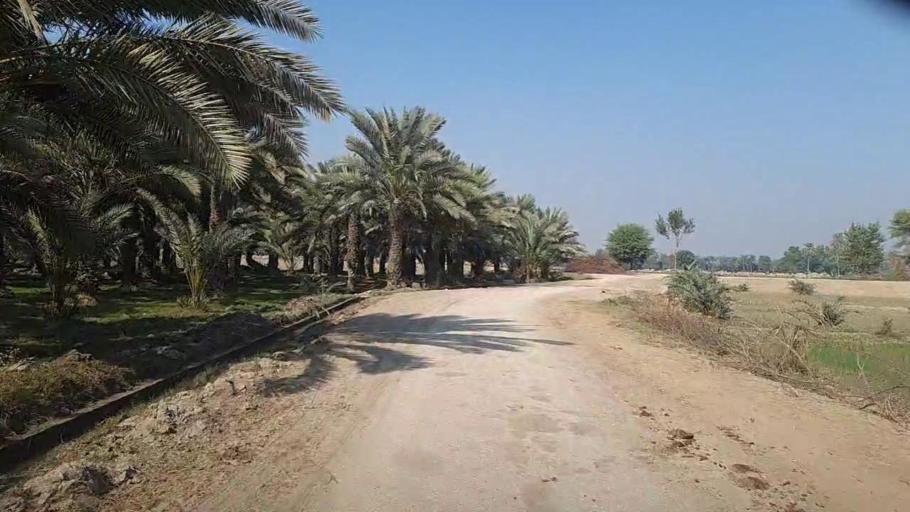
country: PK
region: Sindh
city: Bozdar
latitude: 27.1891
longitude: 68.6116
